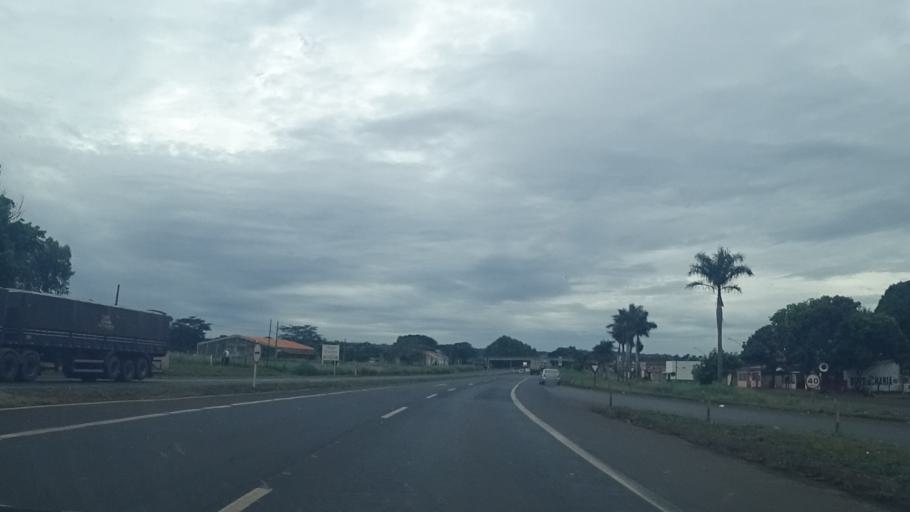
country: BR
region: Minas Gerais
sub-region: Centralina
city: Centralina
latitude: -18.5778
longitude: -49.1936
